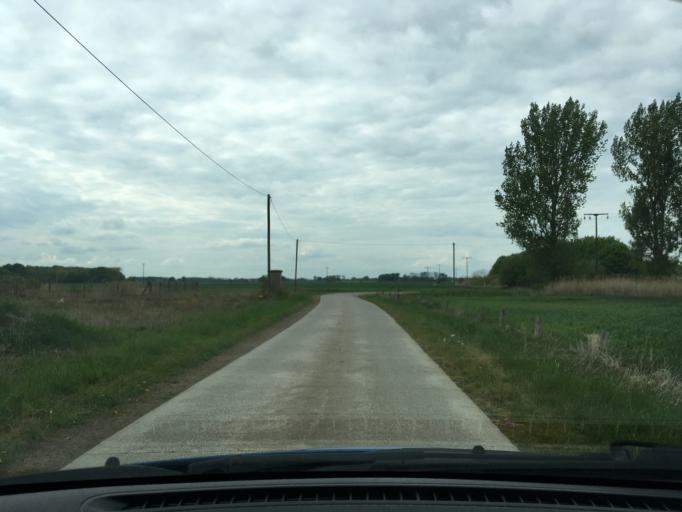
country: DE
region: Lower Saxony
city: Neu Darchau
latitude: 53.2820
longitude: 10.9163
